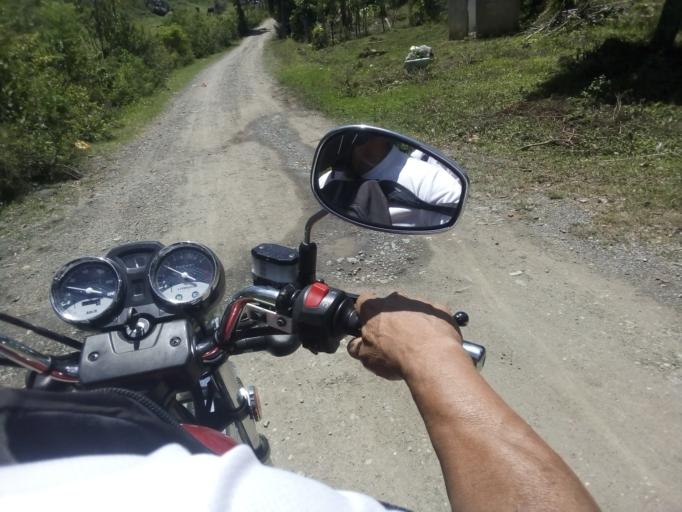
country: CO
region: Santander
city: Guepsa
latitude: 6.0135
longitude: -73.5528
